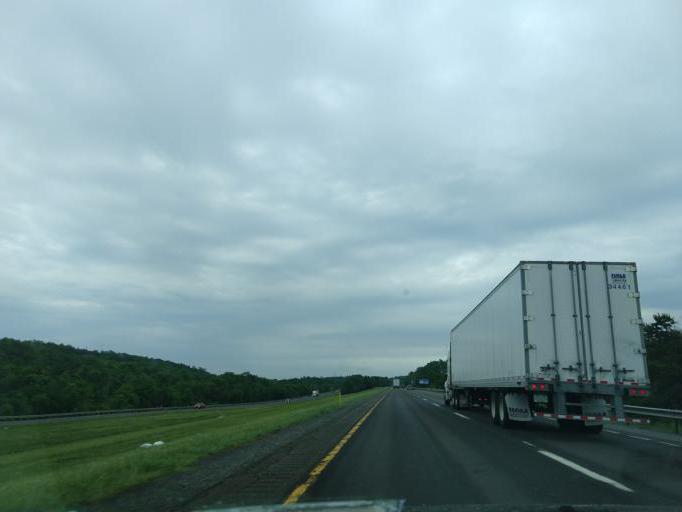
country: US
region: Pennsylvania
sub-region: Luzerne County
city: West Hazleton
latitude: 40.9618
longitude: -76.0280
